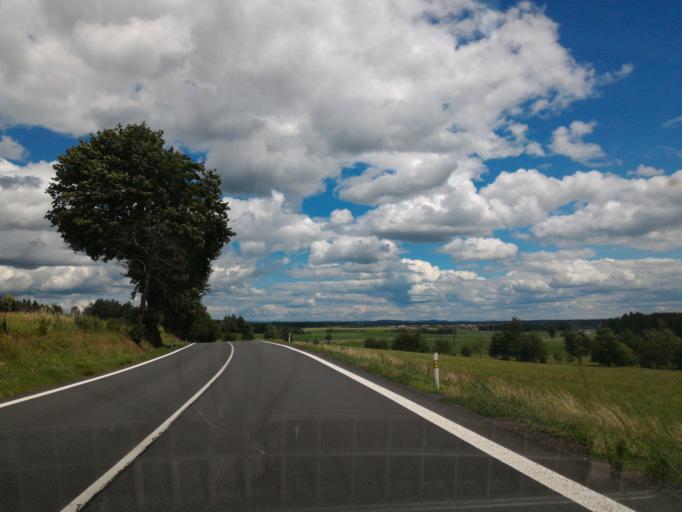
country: CZ
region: Vysocina
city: Bohdalov
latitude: 49.4782
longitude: 15.8362
